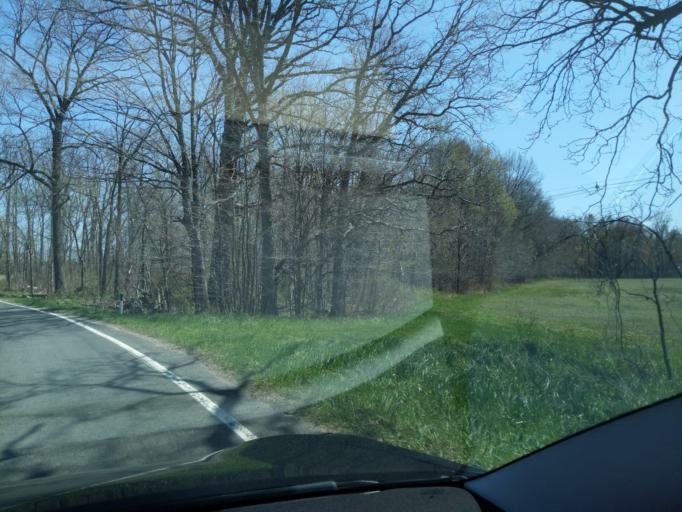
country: US
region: Michigan
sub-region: Ingham County
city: Stockbridge
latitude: 42.4964
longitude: -84.2278
